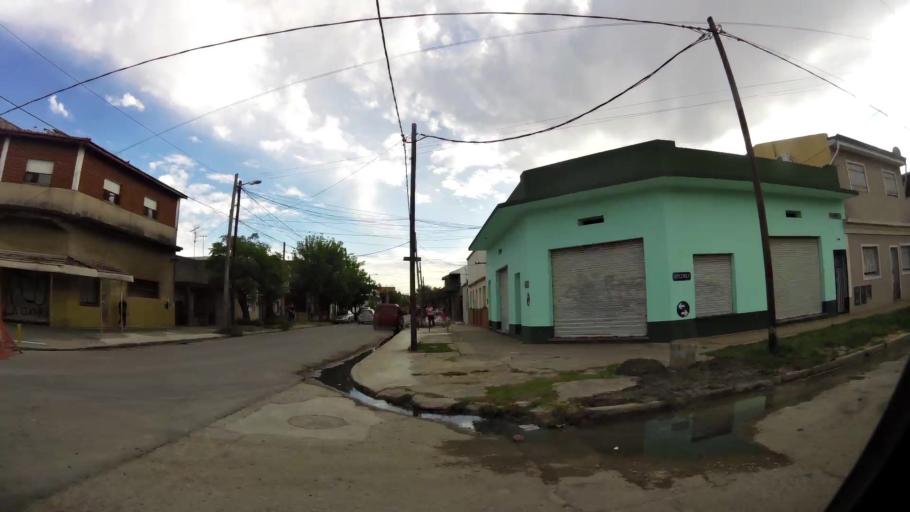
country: AR
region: Buenos Aires
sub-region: Partido de Lanus
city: Lanus
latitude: -34.6969
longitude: -58.3653
